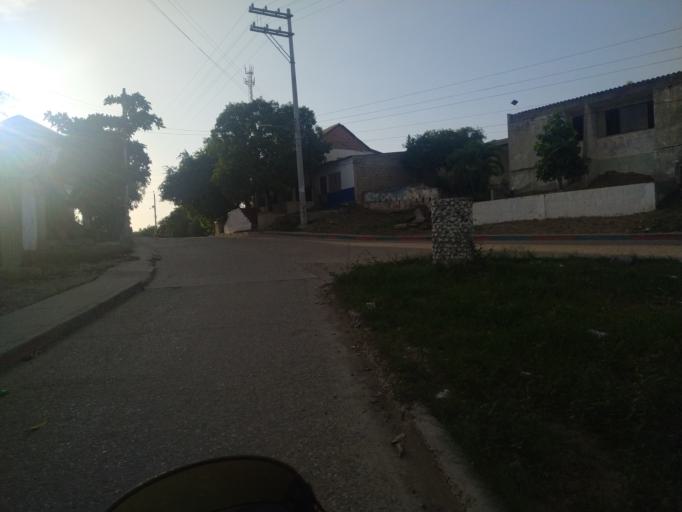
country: CO
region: Bolivar
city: San Estanislao
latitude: 10.3971
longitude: -75.1478
